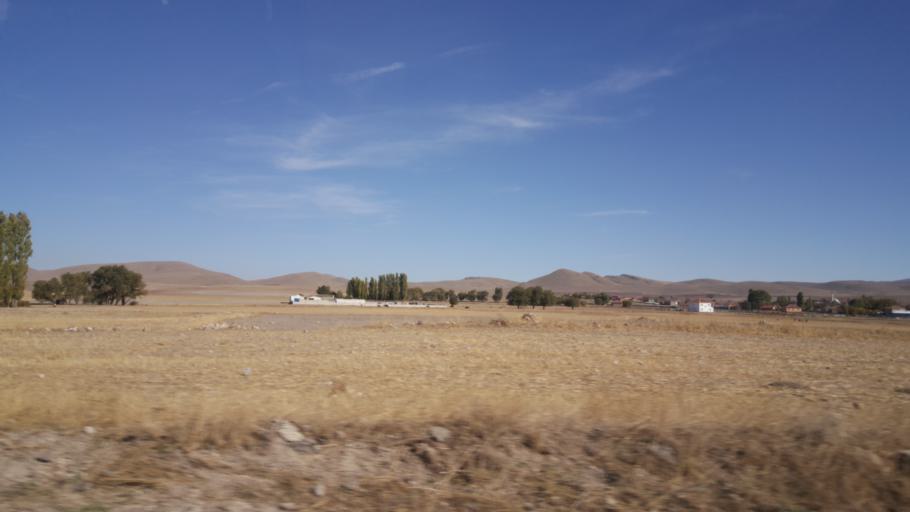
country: TR
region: Ankara
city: Altpinar
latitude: 39.2705
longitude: 32.7544
